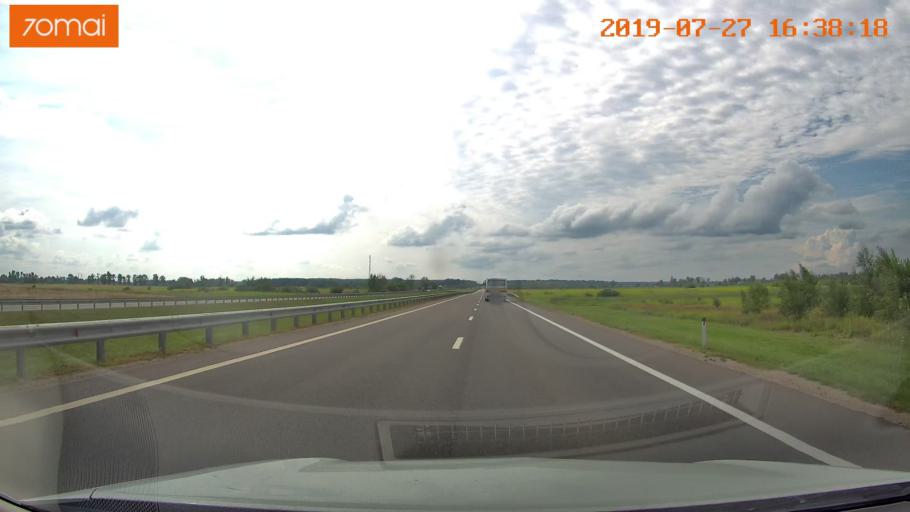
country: RU
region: Kaliningrad
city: Gvardeysk
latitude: 54.6489
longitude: 21.2318
